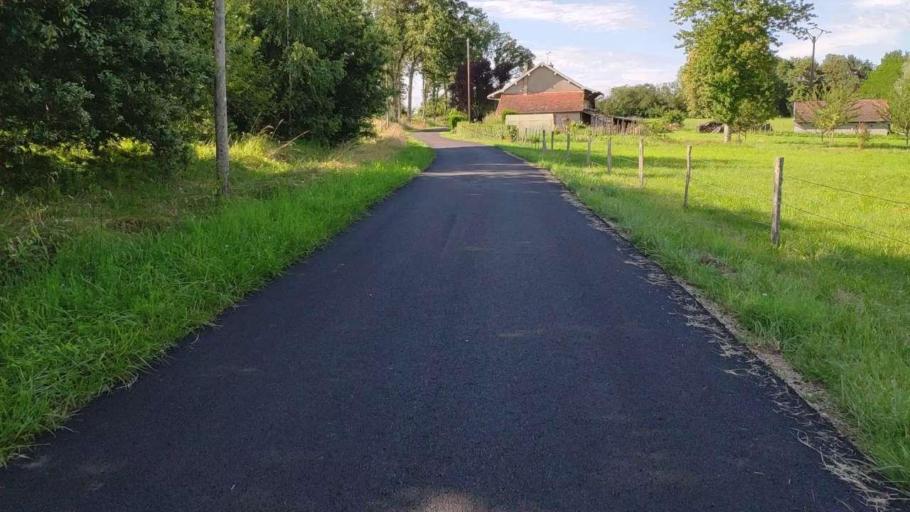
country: FR
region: Franche-Comte
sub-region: Departement du Jura
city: Bletterans
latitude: 46.8270
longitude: 5.5012
